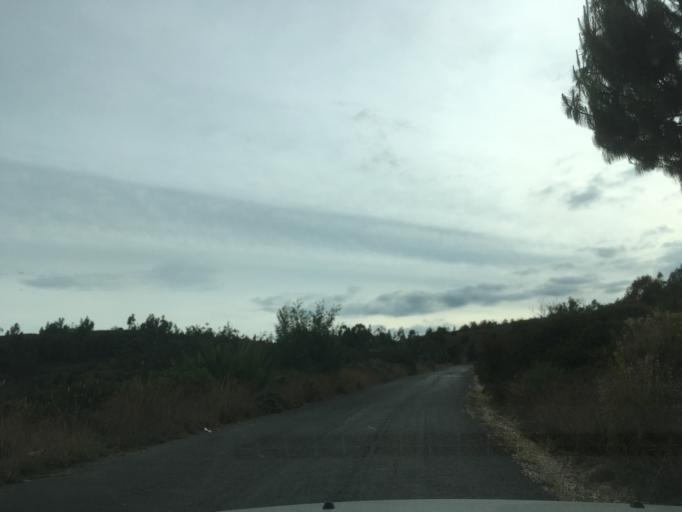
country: CO
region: Boyaca
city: Firavitoba
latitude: 5.6744
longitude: -73.0119
